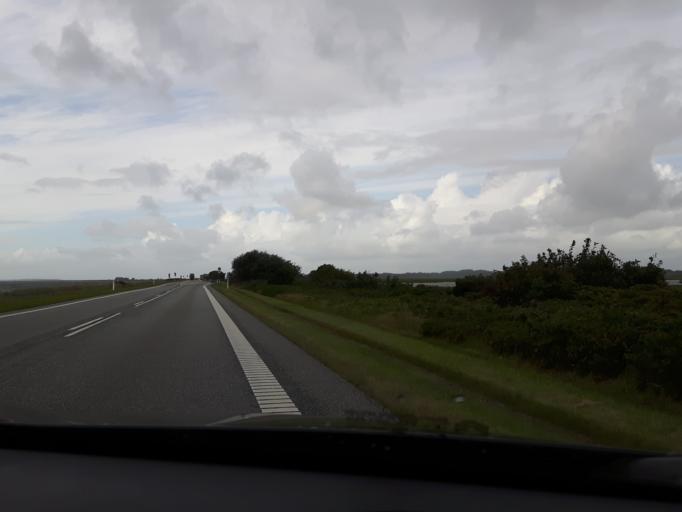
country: DK
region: North Denmark
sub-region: Jammerbugt Kommune
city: Fjerritslev
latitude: 57.0340
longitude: 9.1063
